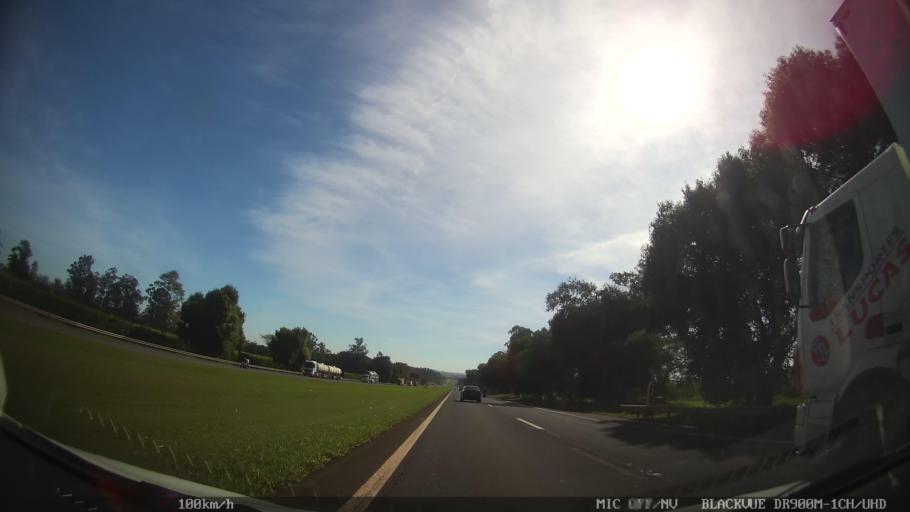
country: BR
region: Sao Paulo
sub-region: Leme
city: Leme
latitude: -22.2408
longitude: -47.3906
